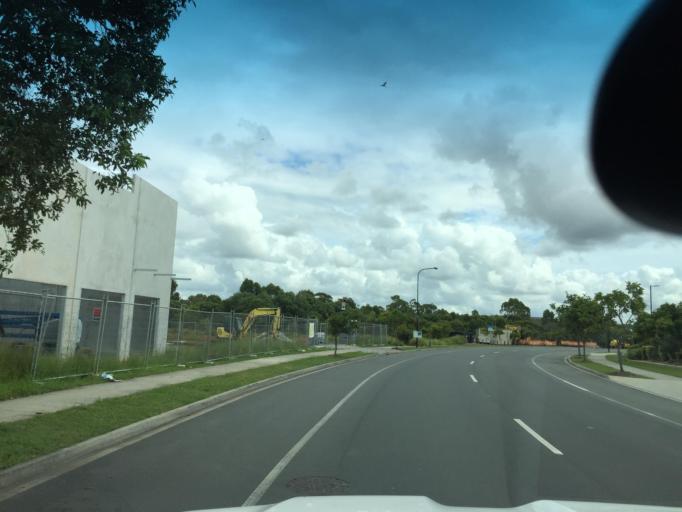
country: AU
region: Queensland
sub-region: Moreton Bay
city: Mango Hill
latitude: -27.2172
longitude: 152.9972
